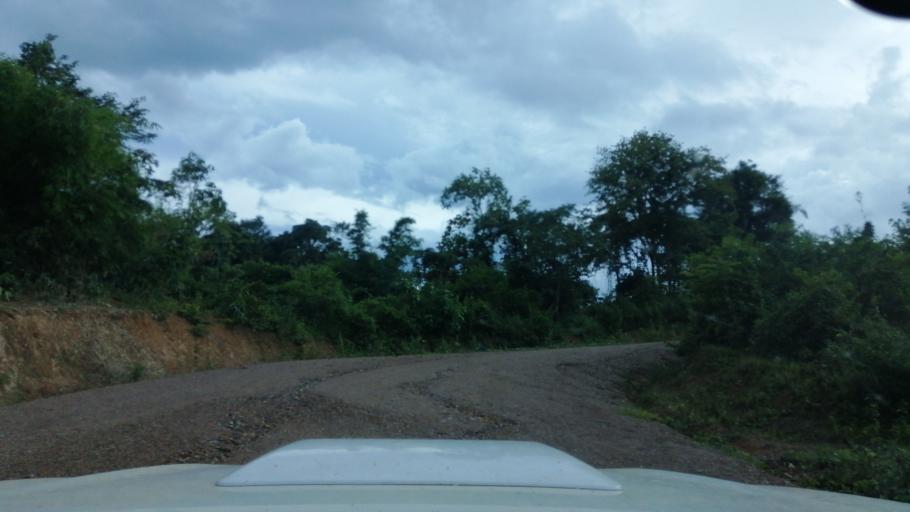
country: TH
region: Nan
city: Song Khwae
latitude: 19.5362
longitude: 100.6998
